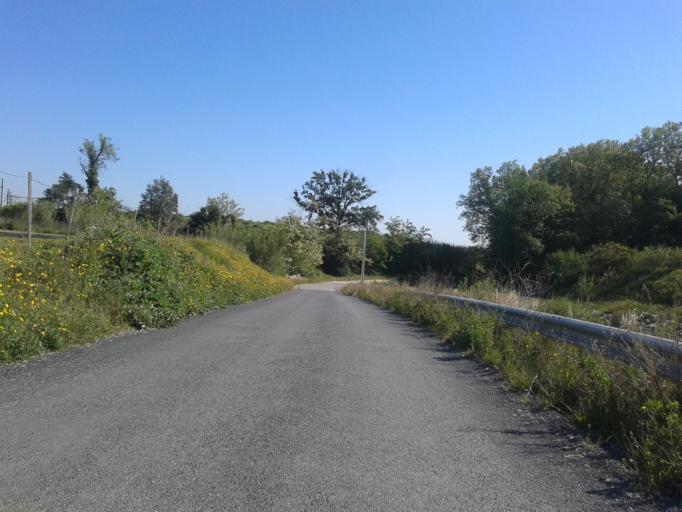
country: FR
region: Languedoc-Roussillon
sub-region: Departement des Pyrenees-Orientales
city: Toulouges
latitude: 42.6737
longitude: 2.8169
